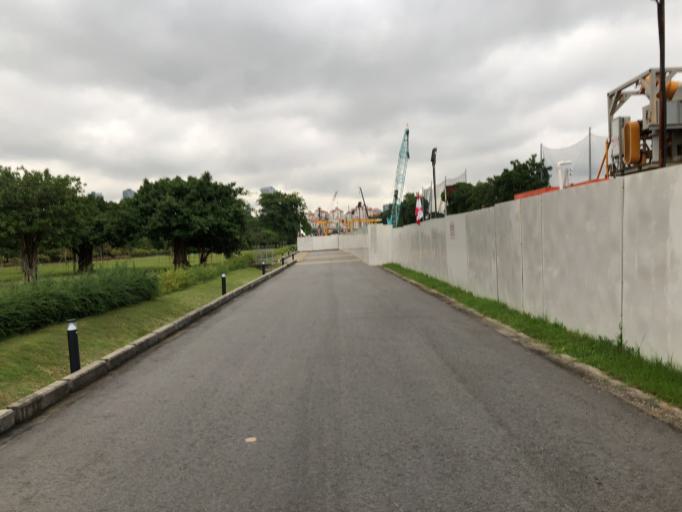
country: SG
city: Singapore
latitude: 1.2871
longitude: 103.8707
